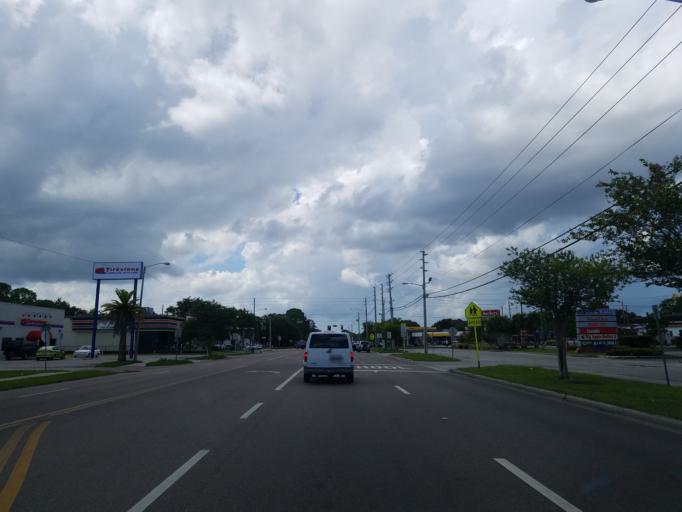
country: US
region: Florida
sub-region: Pinellas County
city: Lealman
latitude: 27.8296
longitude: -82.6469
